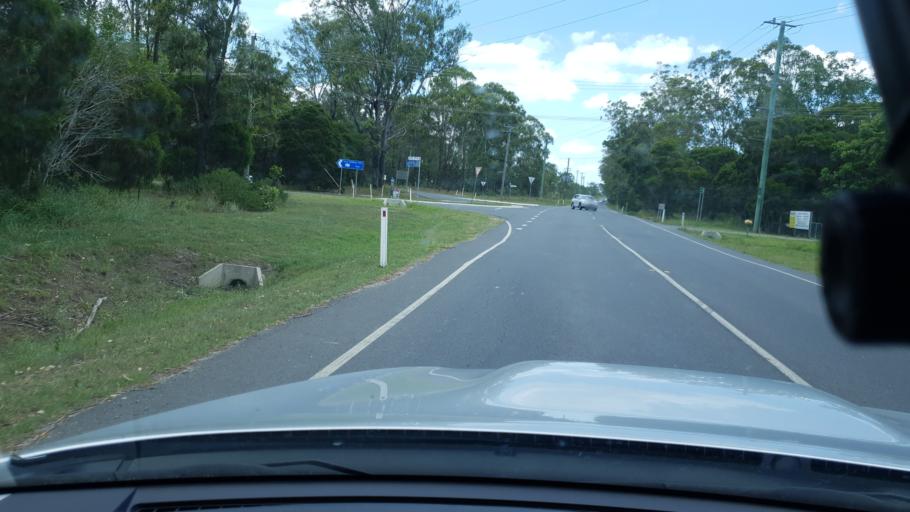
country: AU
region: Queensland
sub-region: Logan
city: North Maclean
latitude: -27.7750
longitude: 153.0092
